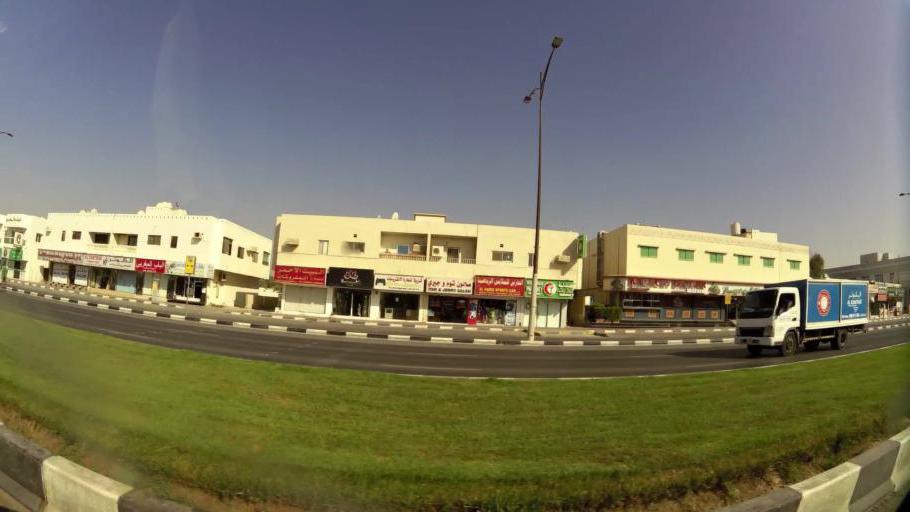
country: AE
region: Ash Shariqah
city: Sharjah
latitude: 25.3353
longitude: 55.4251
